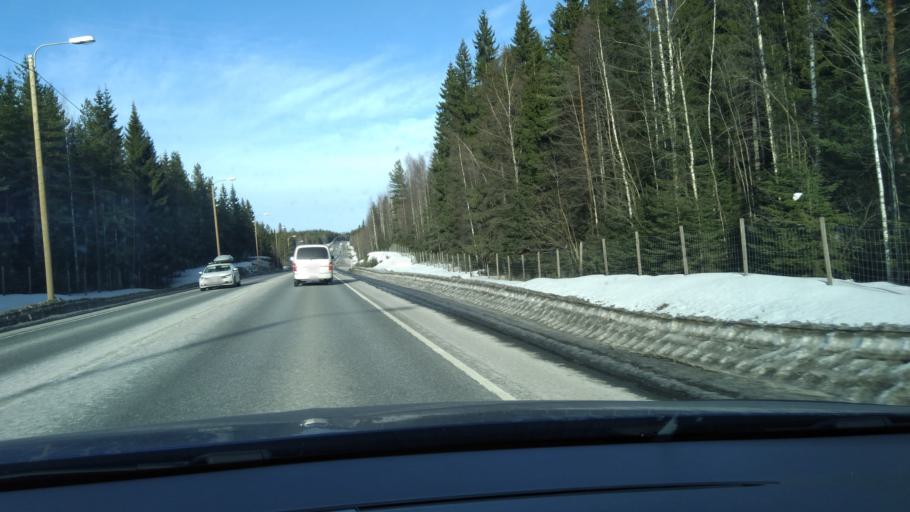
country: FI
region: Pirkanmaa
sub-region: Tampere
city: Orivesi
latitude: 61.6585
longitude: 24.2542
